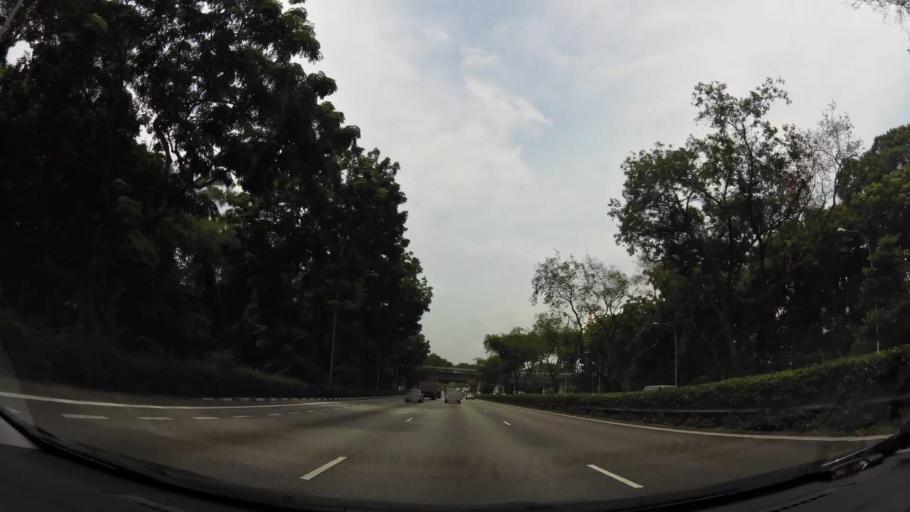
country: SG
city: Singapore
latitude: 1.3665
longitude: 103.9487
